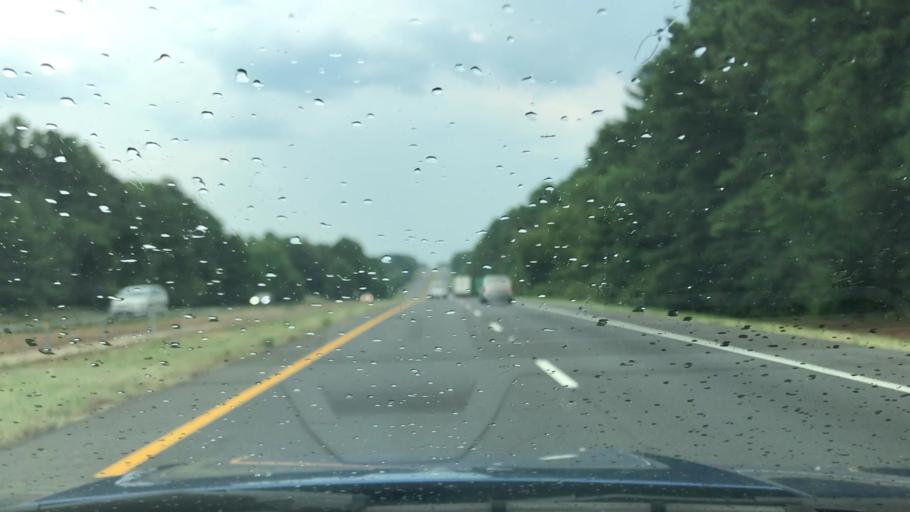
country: US
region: Texas
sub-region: Harrison County
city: Marshall
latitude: 32.4881
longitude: -94.4288
